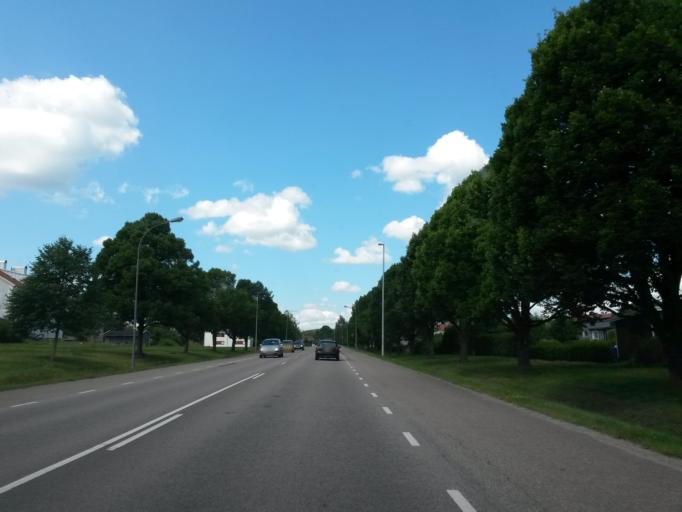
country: SE
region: Vaestra Goetaland
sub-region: Alingsas Kommun
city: Alingsas
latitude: 57.9362
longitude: 12.5414
